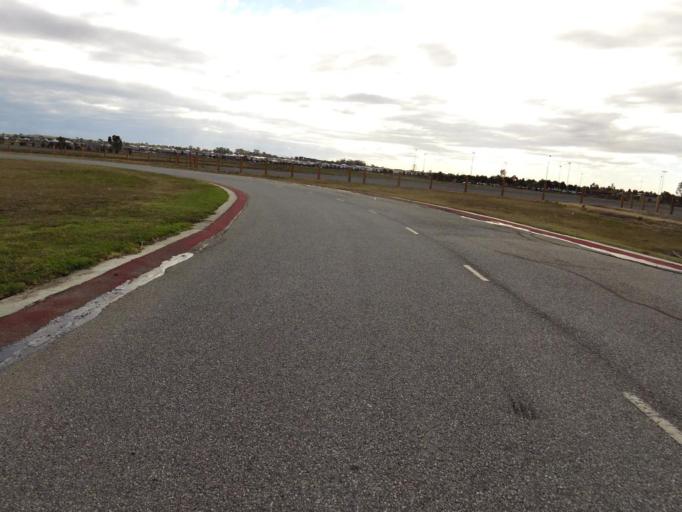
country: AU
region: Victoria
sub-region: Casey
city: Cranbourne East
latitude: -38.1249
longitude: 145.3140
